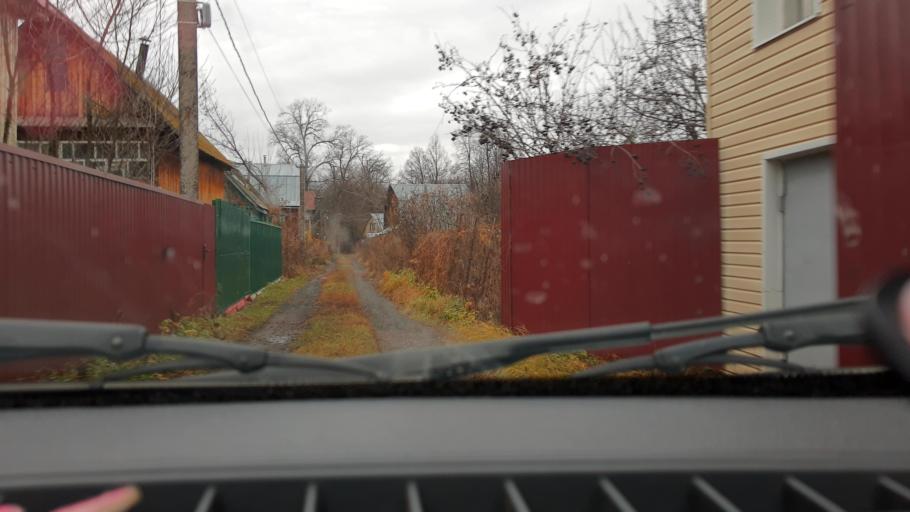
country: RU
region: Bashkortostan
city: Ufa
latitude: 54.6948
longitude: 55.8953
